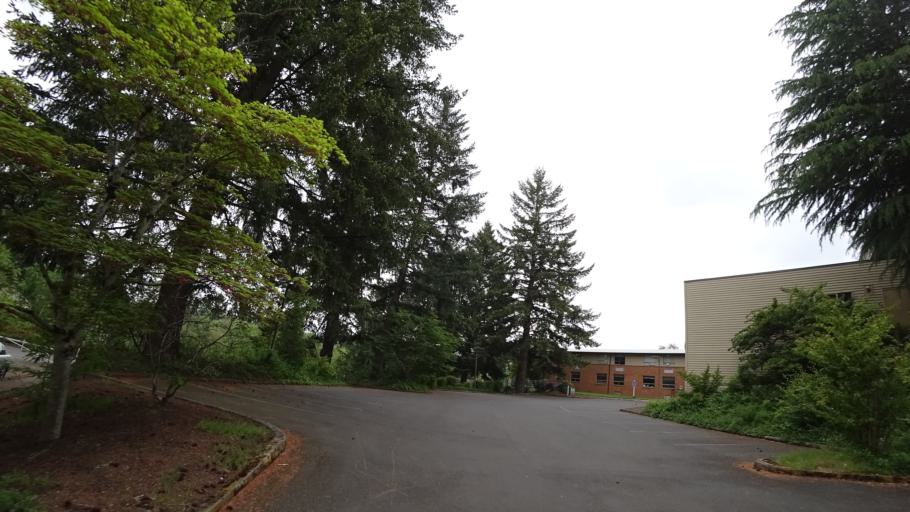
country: US
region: Oregon
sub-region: Washington County
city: West Slope
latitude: 45.4913
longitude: -122.7827
